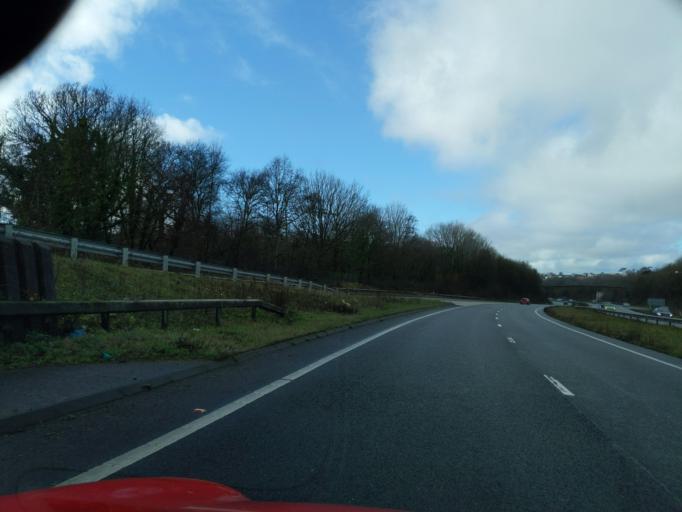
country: GB
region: England
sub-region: Plymouth
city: Plymouth
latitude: 50.4008
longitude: -4.1390
